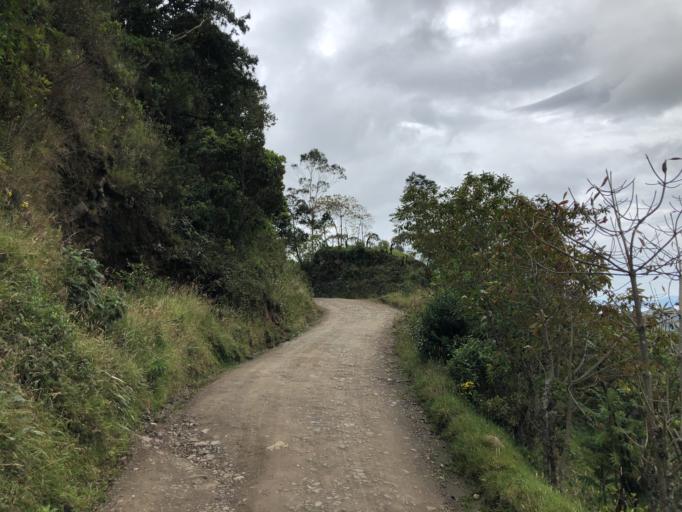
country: CO
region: Cauca
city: Totoro
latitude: 2.5081
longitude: -76.3611
